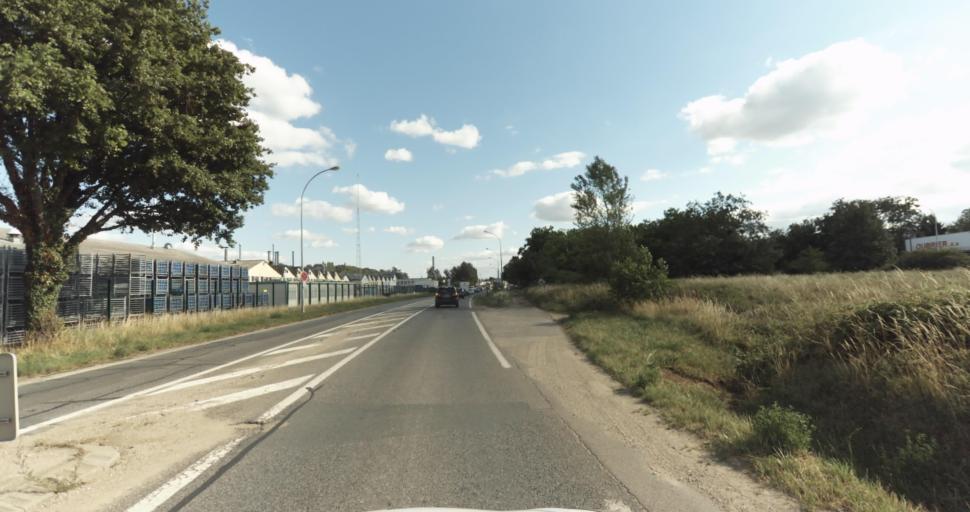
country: FR
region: Rhone-Alpes
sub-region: Departement du Rhone
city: Chaponost
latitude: 45.7038
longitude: 4.7678
